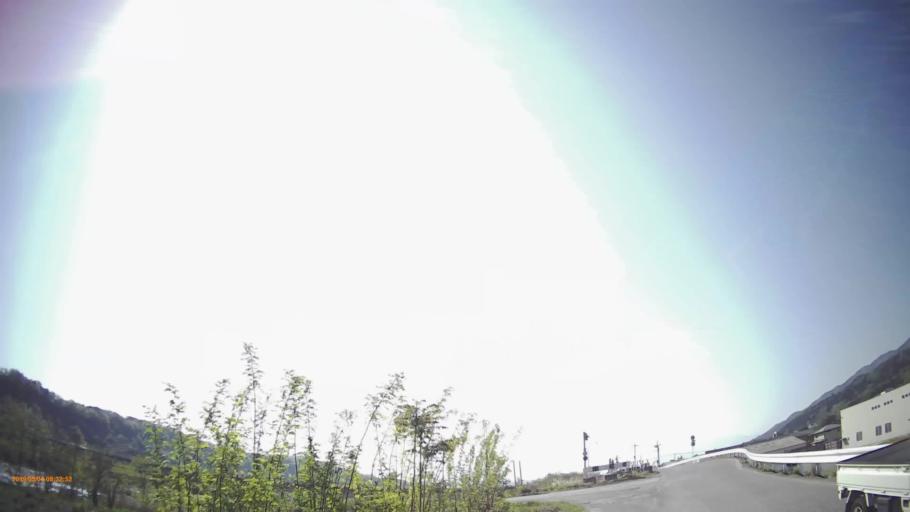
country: JP
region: Yamanashi
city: Nirasaki
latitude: 35.7315
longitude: 138.4174
